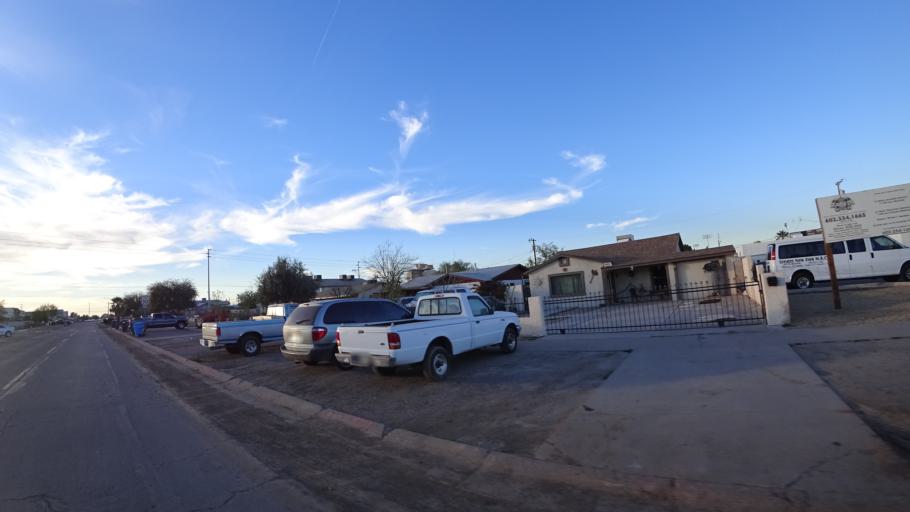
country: US
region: Arizona
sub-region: Maricopa County
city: Phoenix
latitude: 33.4312
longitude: -112.0794
